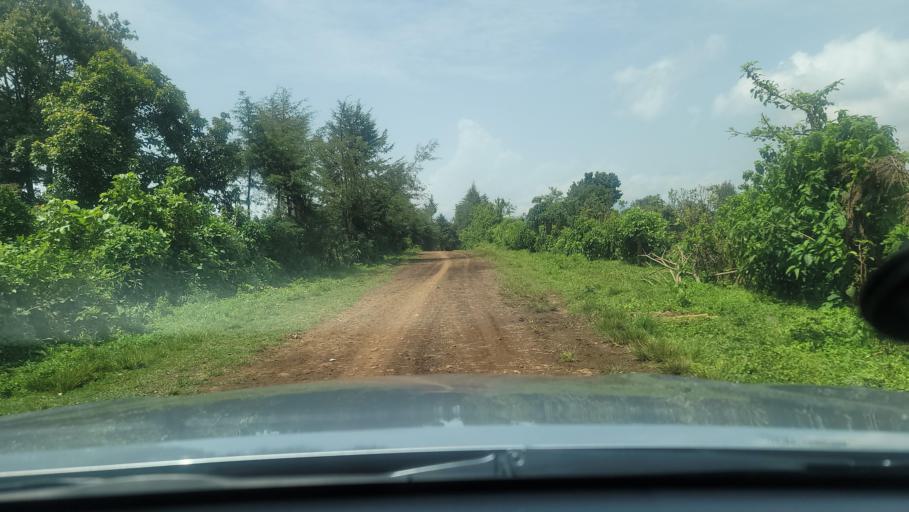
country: ET
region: Oromiya
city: Agaro
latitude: 7.8336
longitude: 36.4054
